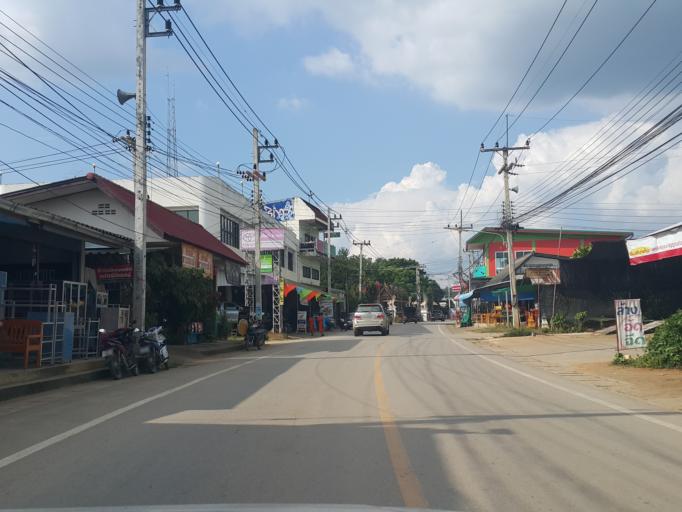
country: TH
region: Chiang Mai
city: Mae Chaem
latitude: 18.5046
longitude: 98.3602
